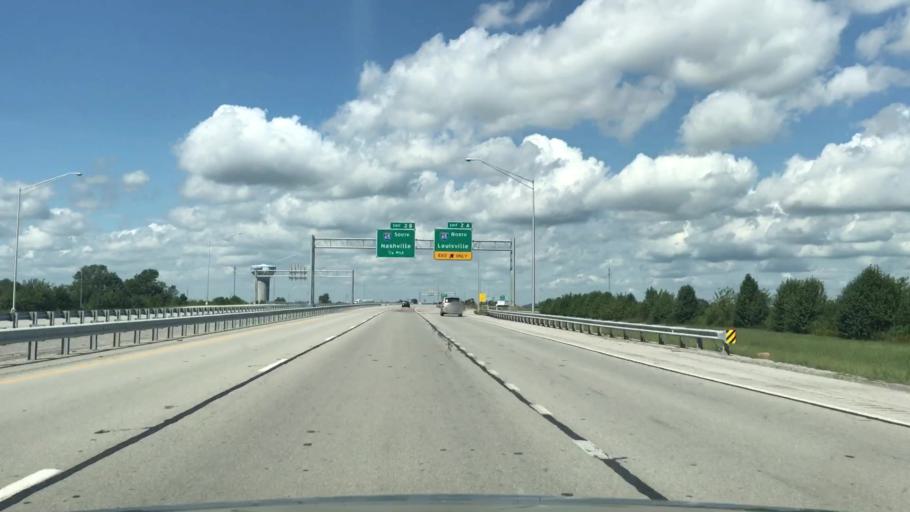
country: US
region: Kentucky
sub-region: Warren County
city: Plano
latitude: 36.9088
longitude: -86.4249
